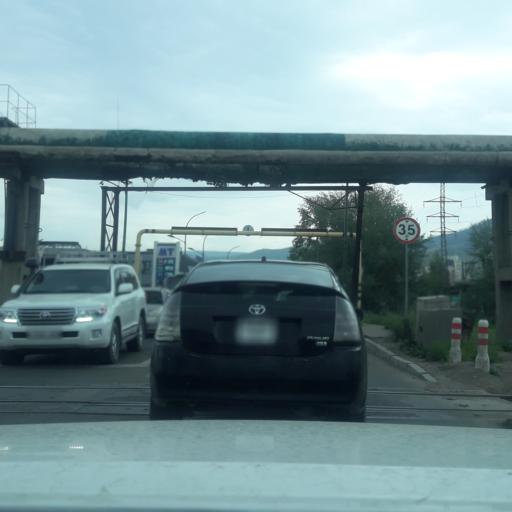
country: MN
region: Ulaanbaatar
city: Ulaanbaatar
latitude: 47.8980
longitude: 106.8697
